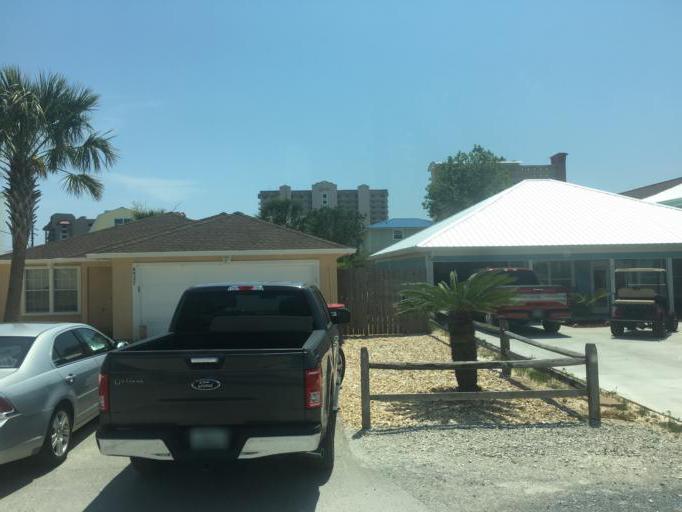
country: US
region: Florida
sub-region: Bay County
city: Lower Grand Lagoon
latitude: 30.1547
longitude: -85.7667
